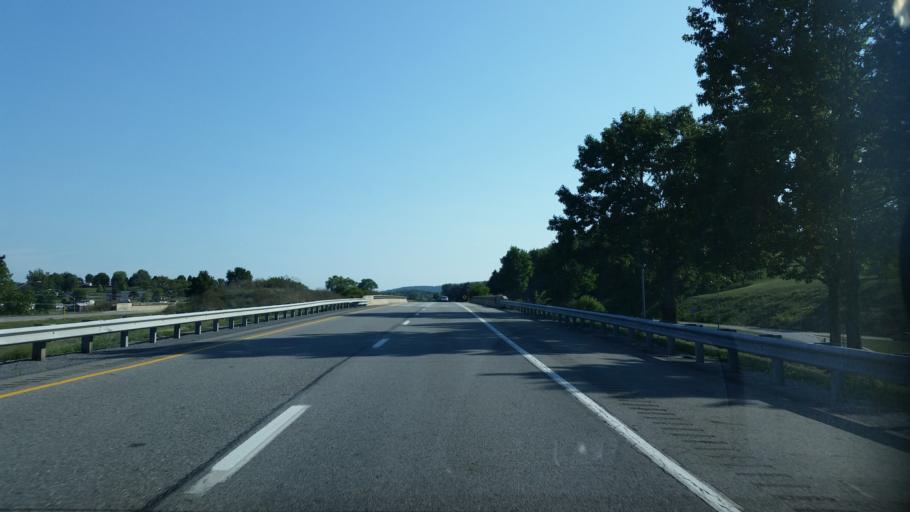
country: US
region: Pennsylvania
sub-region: Bedford County
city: Bedford
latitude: 40.0972
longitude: -78.5293
